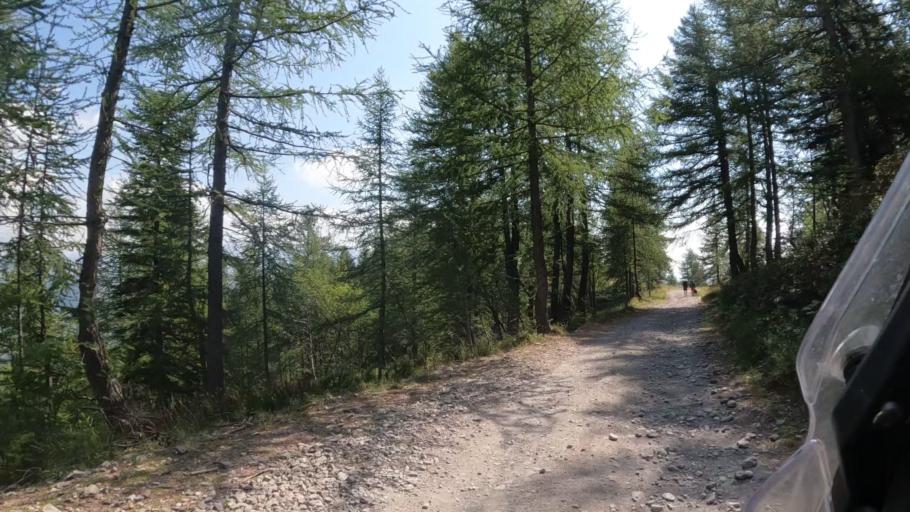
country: IT
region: Piedmont
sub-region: Provincia di Cuneo
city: Briga Alta
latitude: 44.1030
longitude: 7.7174
